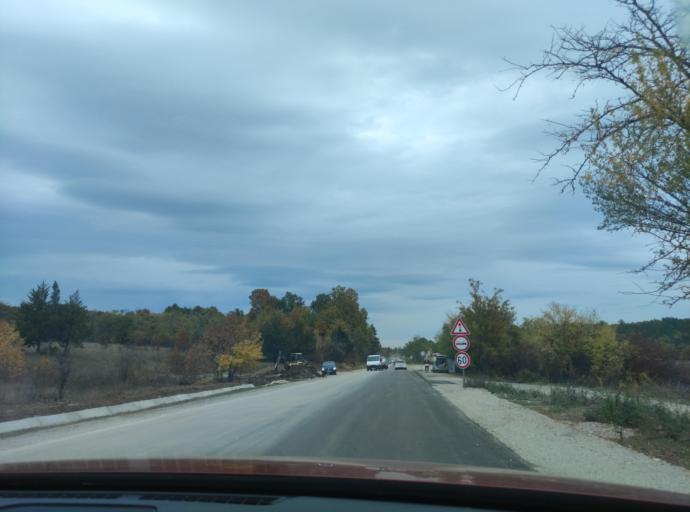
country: BG
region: Montana
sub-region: Obshtina Montana
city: Montana
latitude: 43.3810
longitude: 23.2422
